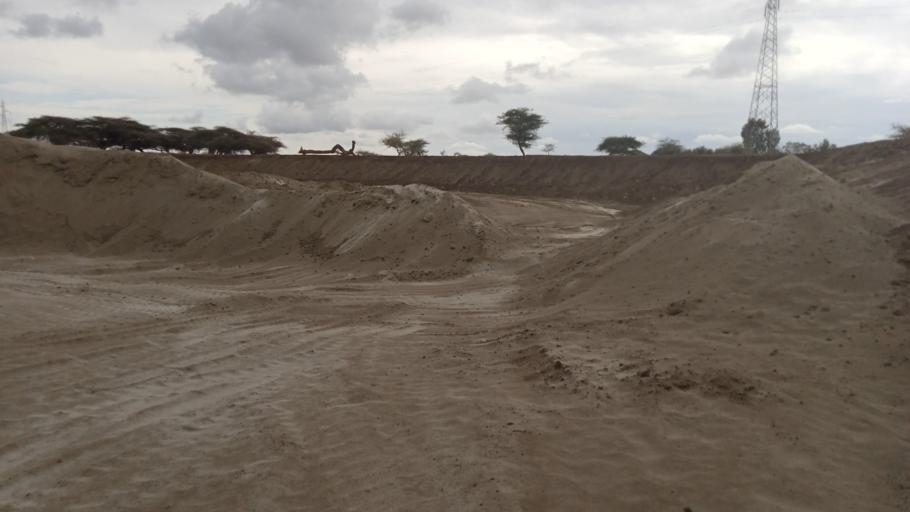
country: ET
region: Oromiya
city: Ziway
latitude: 7.9208
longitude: 38.6797
